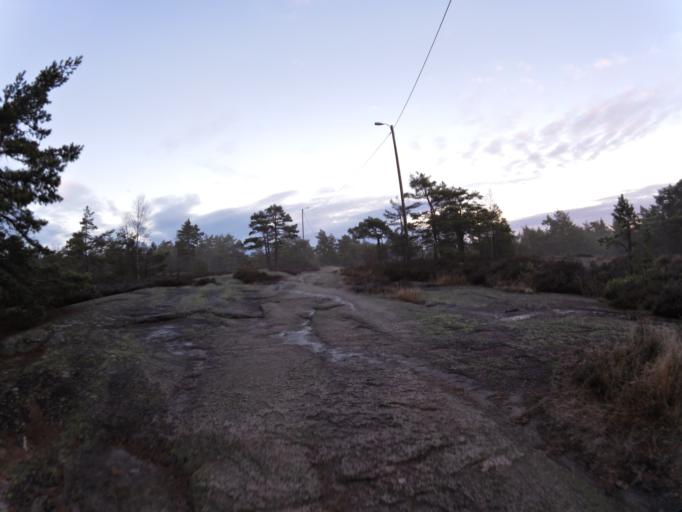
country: NO
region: Ostfold
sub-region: Fredrikstad
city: Fredrikstad
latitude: 59.2634
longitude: 10.9723
